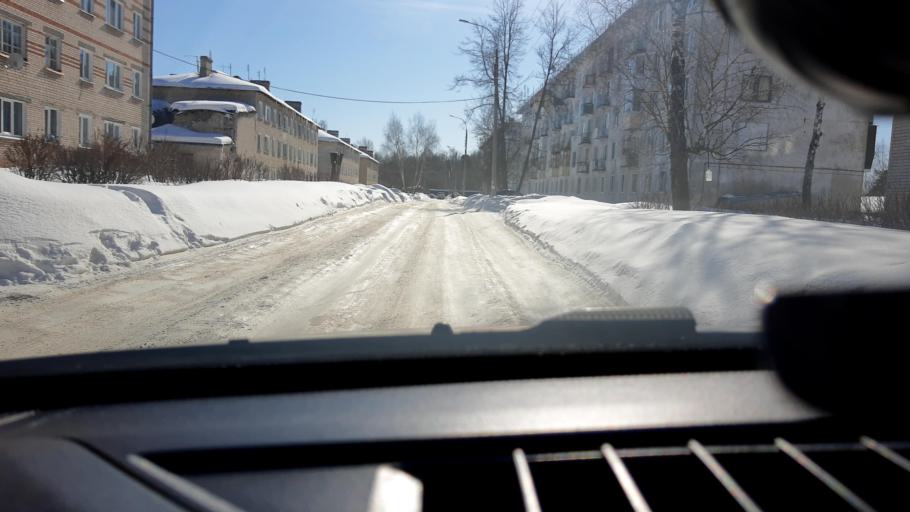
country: RU
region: Nizjnij Novgorod
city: Yuganets
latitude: 56.2479
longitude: 43.2288
